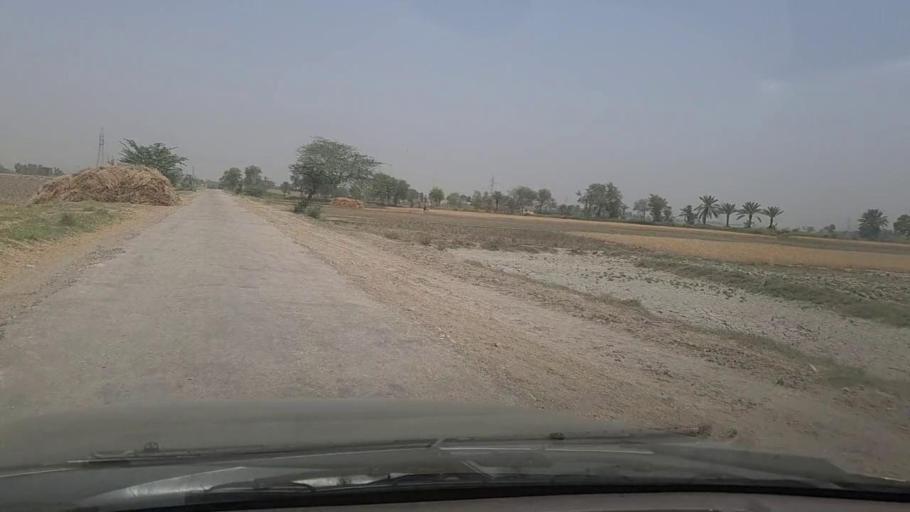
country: PK
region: Sindh
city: Madeji
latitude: 27.8212
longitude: 68.3962
